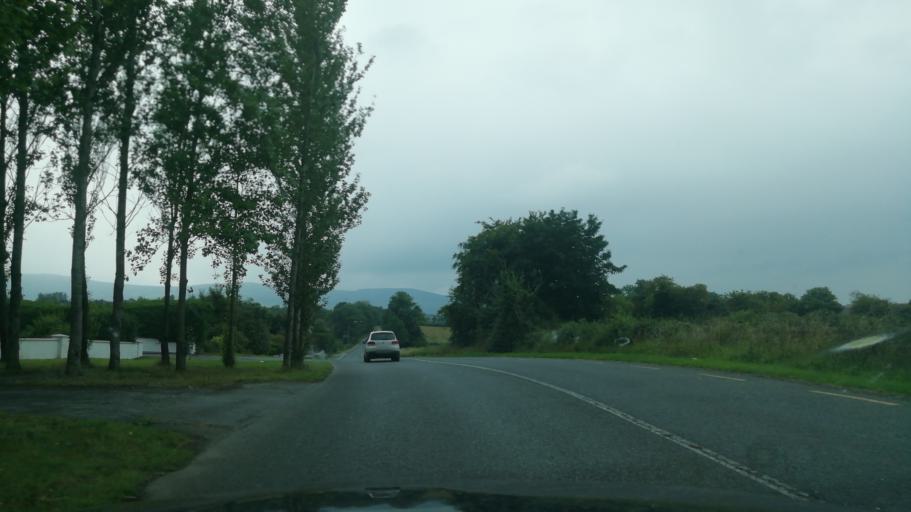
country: IE
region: Munster
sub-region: South Tipperary
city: Cluain Meala
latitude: 52.3760
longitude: -7.6983
